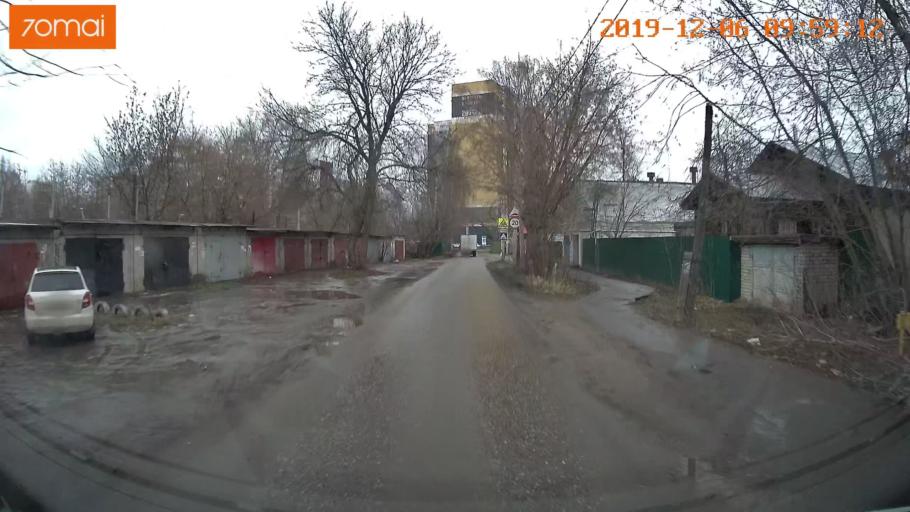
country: RU
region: Ivanovo
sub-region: Gorod Ivanovo
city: Ivanovo
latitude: 56.9850
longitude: 40.9772
